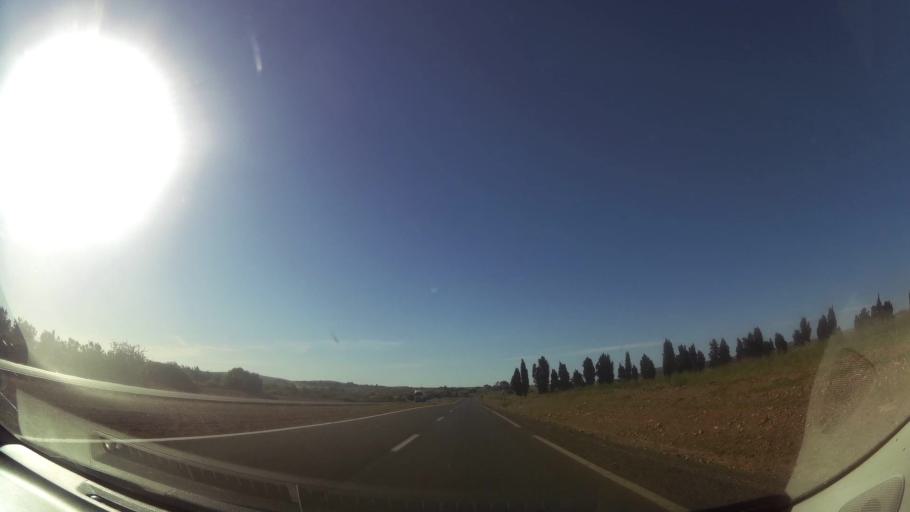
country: MA
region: Oriental
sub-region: Berkane-Taourirt
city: Ahfir
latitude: 35.0234
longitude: -2.2047
